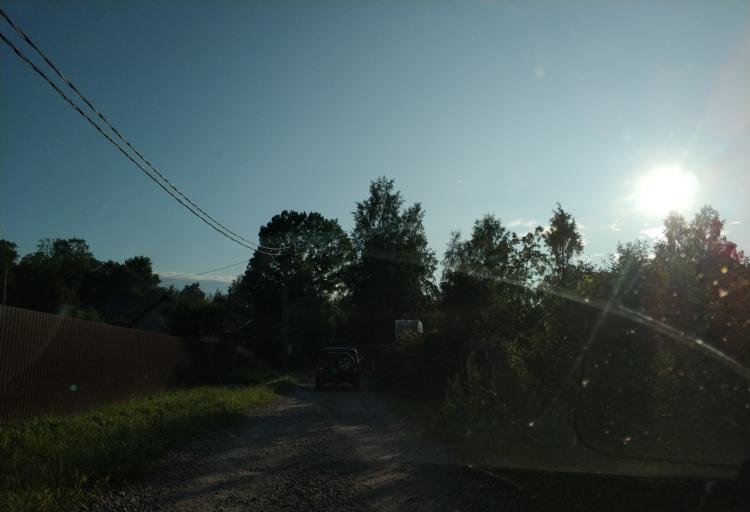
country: RU
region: Leningrad
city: Sapernoye
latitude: 60.6952
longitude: 29.9843
